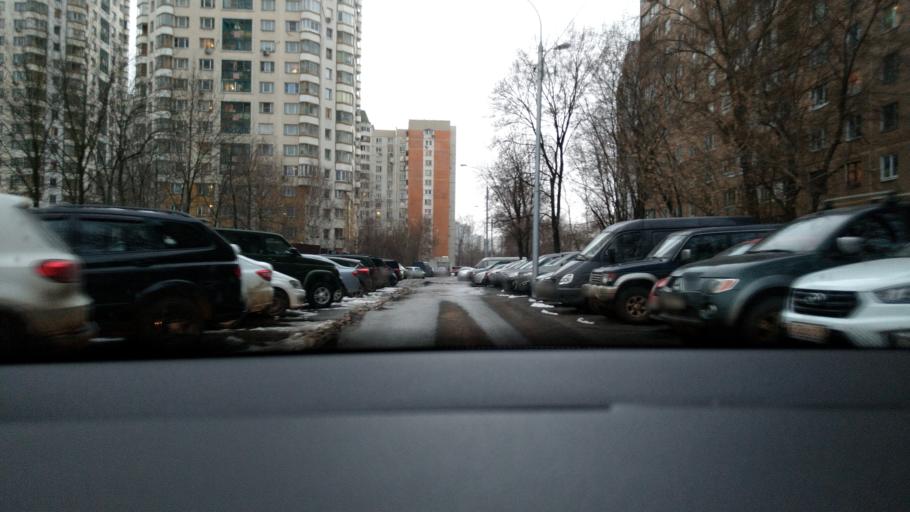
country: RU
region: Moscow
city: Brateyevo
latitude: 55.6327
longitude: 37.7556
